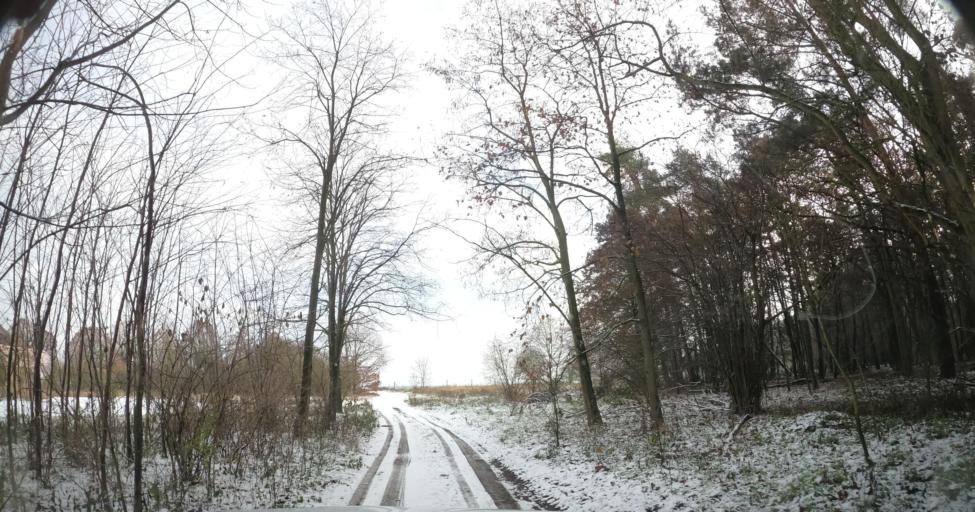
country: PL
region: West Pomeranian Voivodeship
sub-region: Powiat gryfinski
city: Mieszkowice
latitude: 52.7370
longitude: 14.4910
